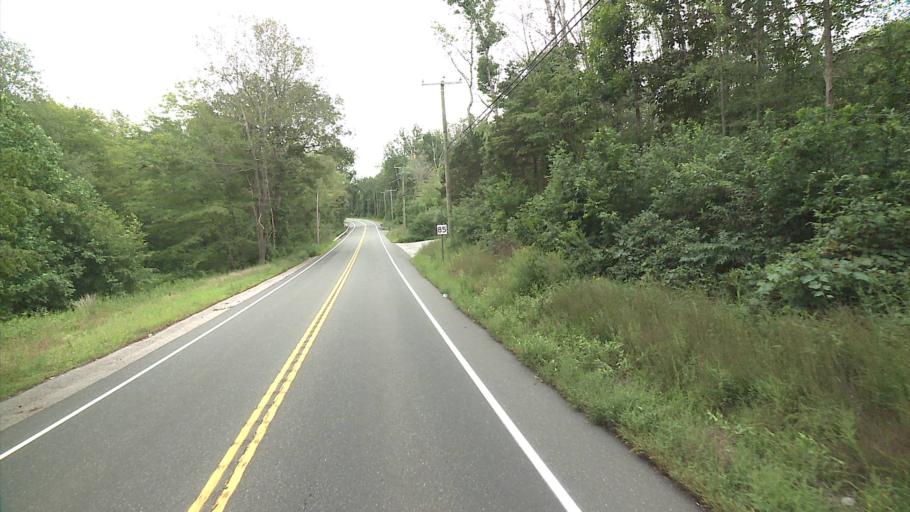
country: US
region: Connecticut
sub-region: New London County
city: Colchester
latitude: 41.5054
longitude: -72.2884
